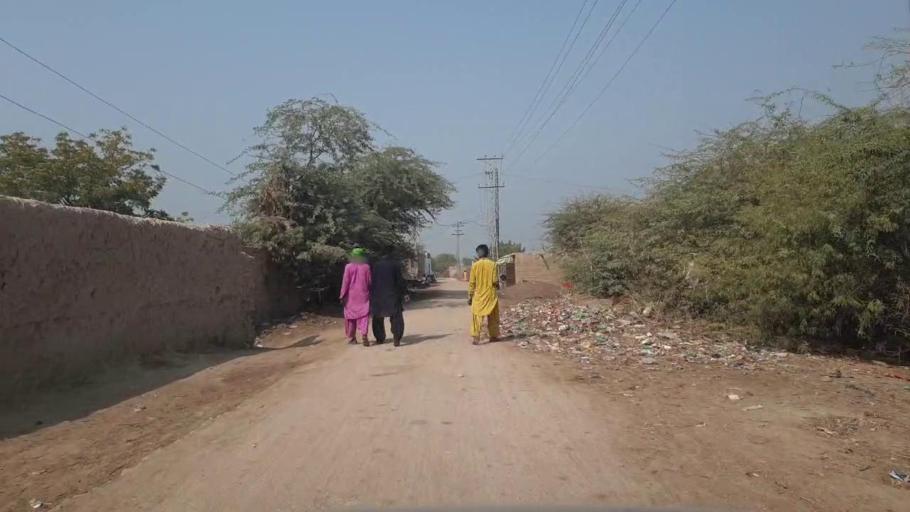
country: PK
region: Sindh
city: Hala
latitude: 25.8110
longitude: 68.4131
